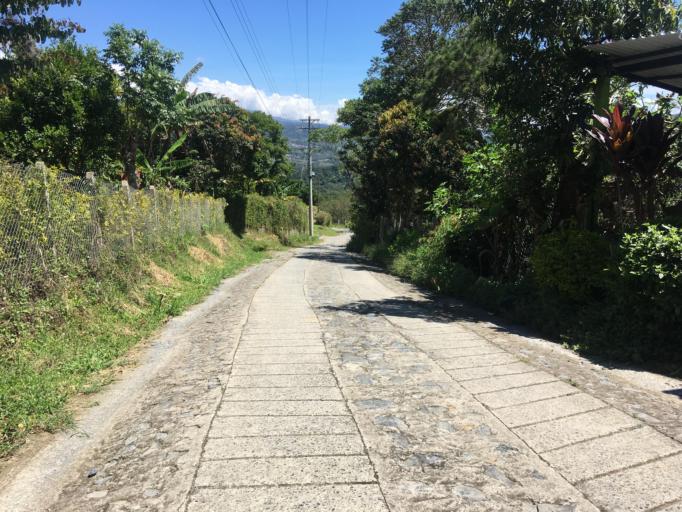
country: CO
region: Santander
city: Barbosa
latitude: 5.9145
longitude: -73.5983
